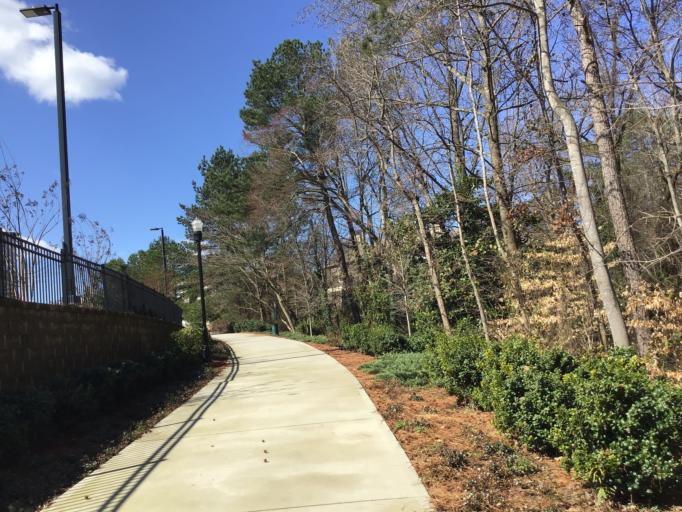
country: US
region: Georgia
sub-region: DeKalb County
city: Chamblee
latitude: 33.8894
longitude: -84.3150
